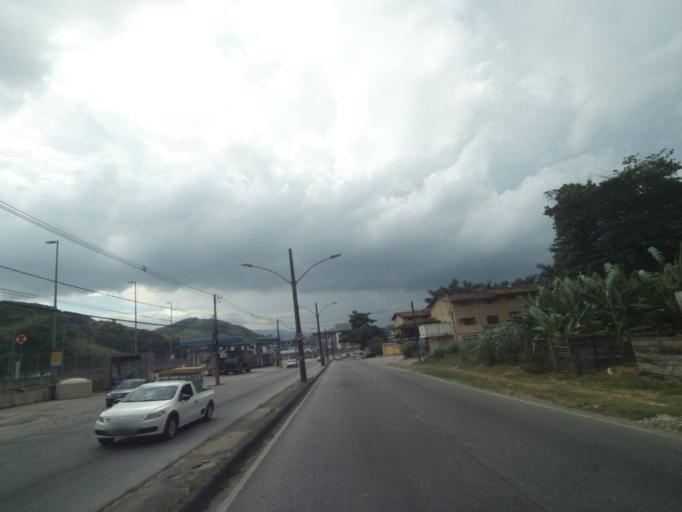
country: BR
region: Rio de Janeiro
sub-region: Nilopolis
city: Nilopolis
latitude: -22.8979
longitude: -43.3976
